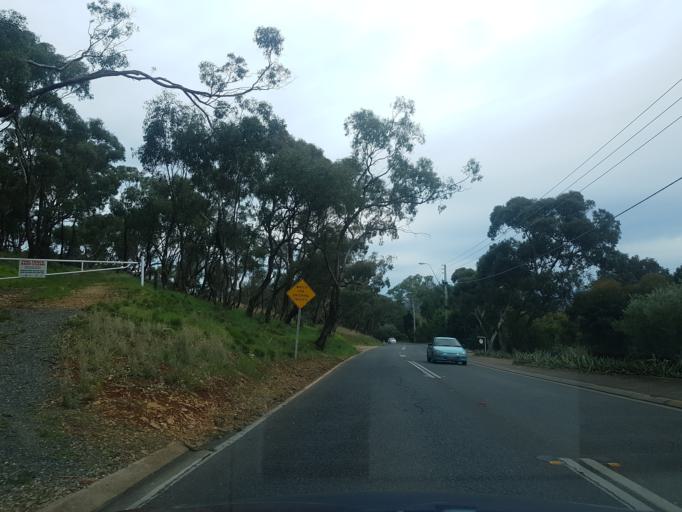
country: AU
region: South Australia
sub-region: Mitcham
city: Mitcham
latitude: -34.9864
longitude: 138.6239
